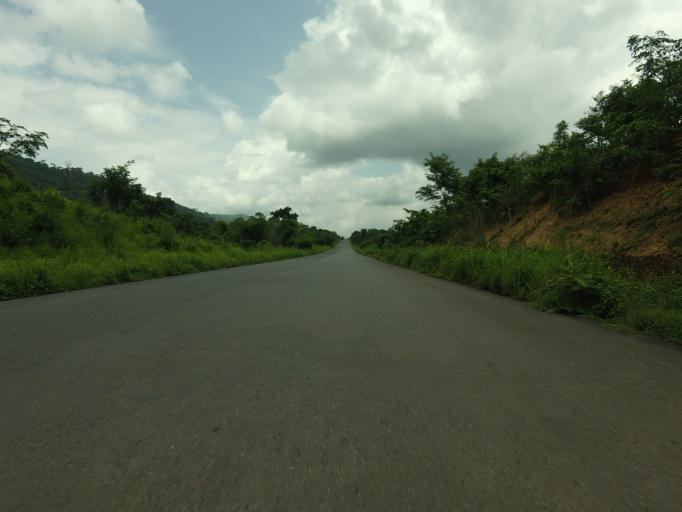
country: GH
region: Volta
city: Ho
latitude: 6.6125
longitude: 0.3012
